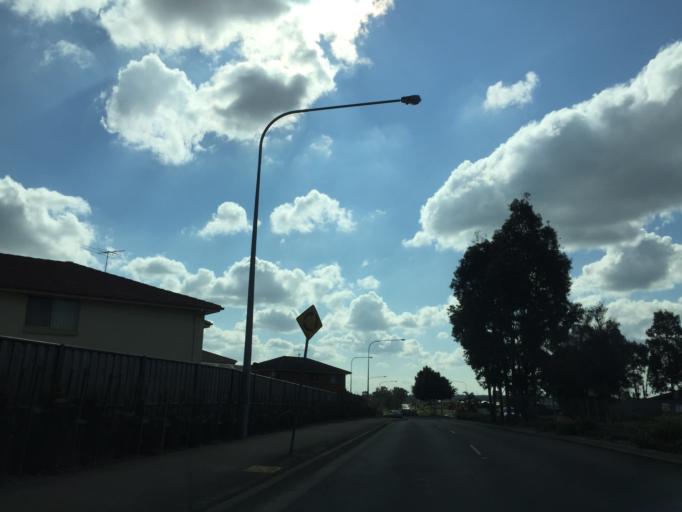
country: AU
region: New South Wales
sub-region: Blacktown
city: Quakers Hill
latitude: -33.7142
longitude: 150.8930
